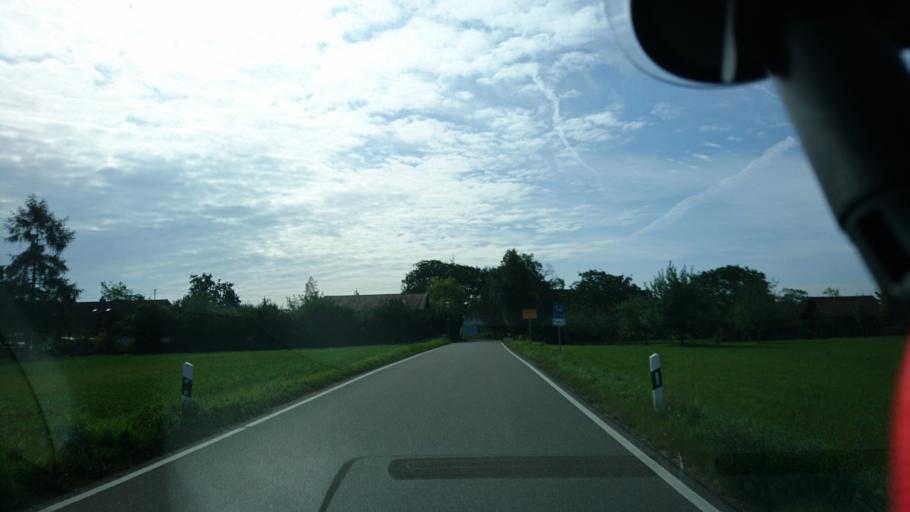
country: DE
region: Baden-Wuerttemberg
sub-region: Regierungsbezirk Stuttgart
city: Mainhardt
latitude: 49.0923
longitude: 9.5755
